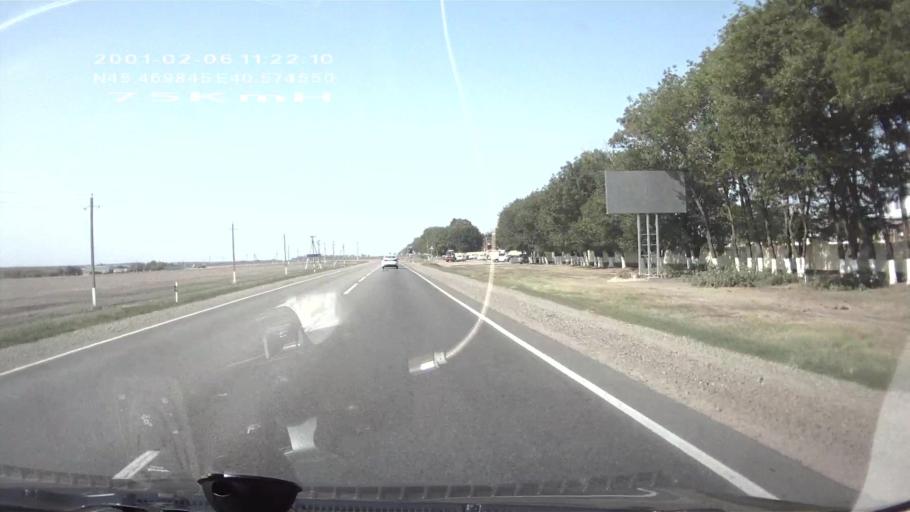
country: RU
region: Krasnodarskiy
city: Kropotkin
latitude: 45.4699
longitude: 40.5734
